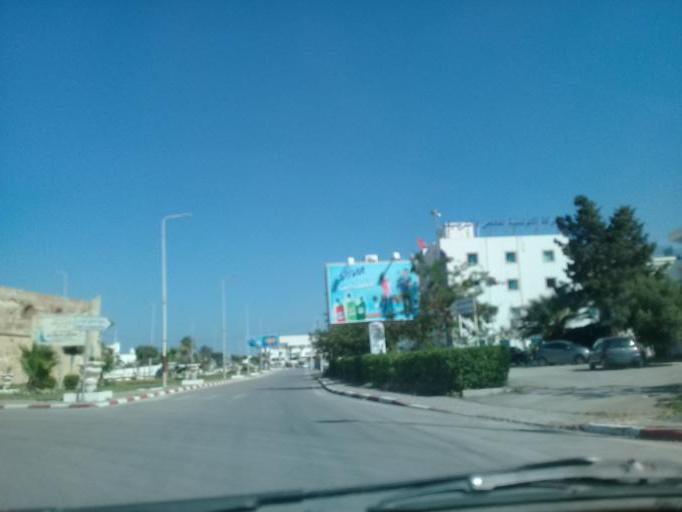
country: TN
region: Tunis
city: La Goulette
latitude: 36.8139
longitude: 10.3020
